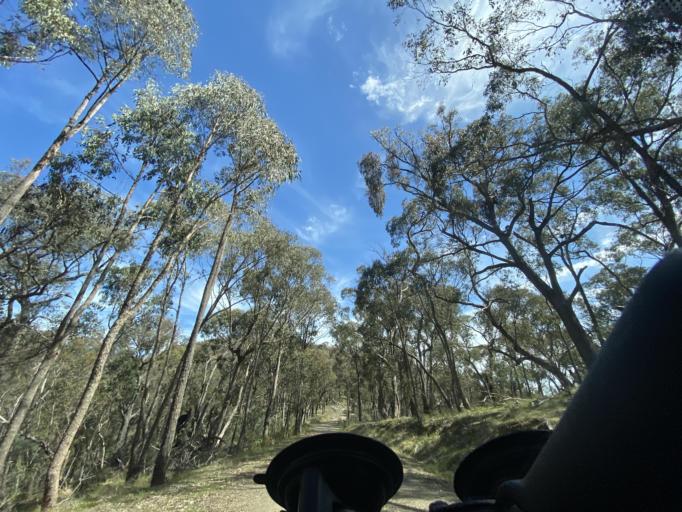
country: AU
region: Victoria
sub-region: Mansfield
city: Mansfield
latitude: -36.8027
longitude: 146.1100
